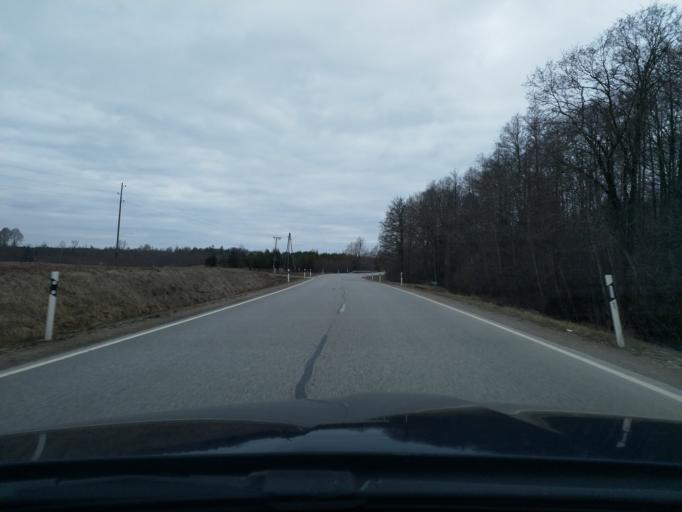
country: LV
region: Kuldigas Rajons
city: Kuldiga
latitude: 56.9620
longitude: 22.0742
